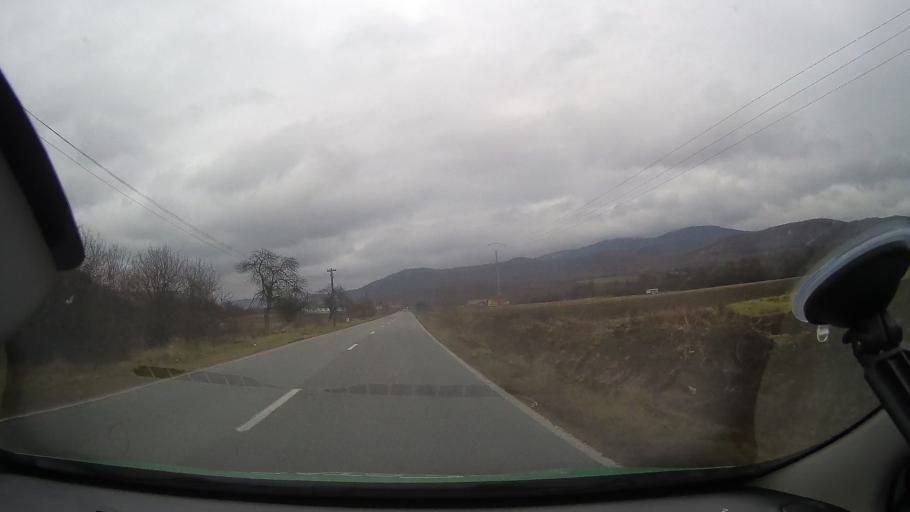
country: RO
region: Arad
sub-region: Comuna Buteni
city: Buteni
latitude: 46.3143
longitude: 22.1395
